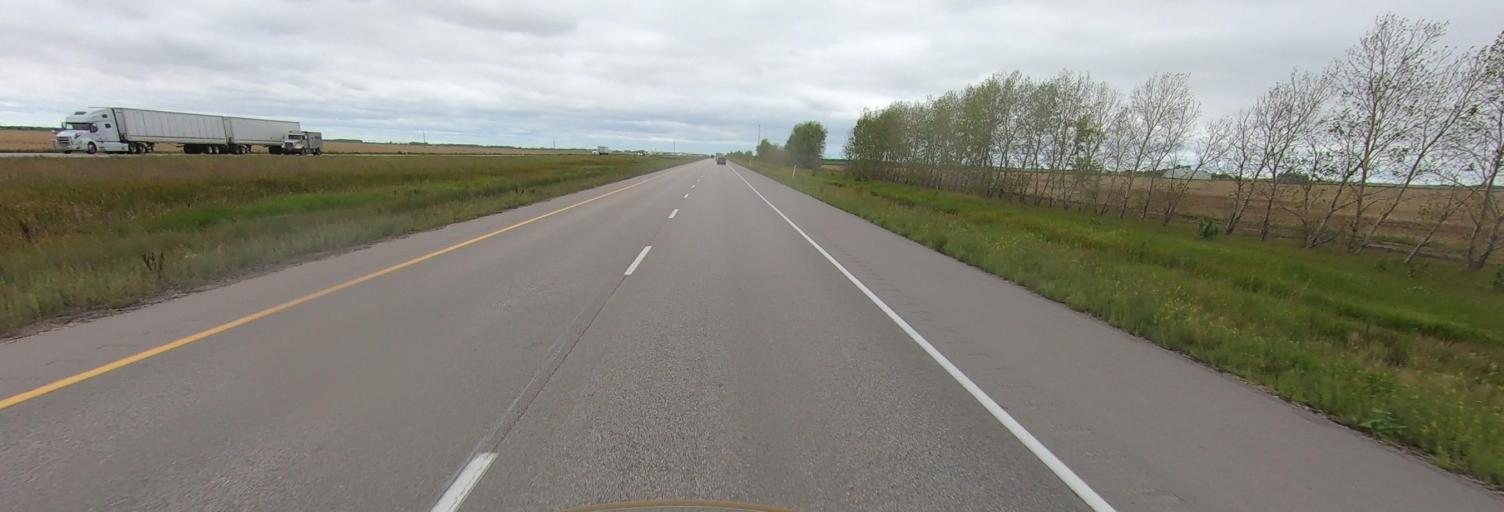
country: CA
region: Manitoba
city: Headingley
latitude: 49.8927
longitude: -97.6808
